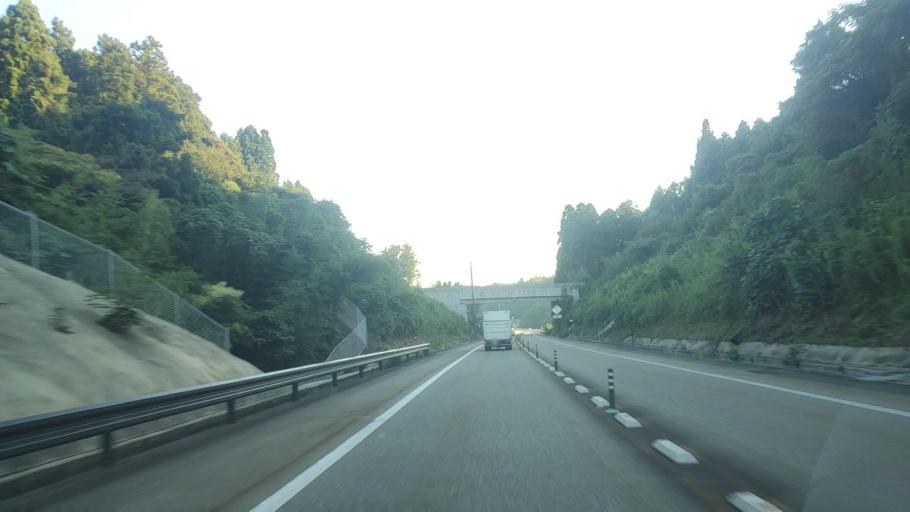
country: JP
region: Ishikawa
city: Nanao
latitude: 36.9842
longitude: 137.0471
